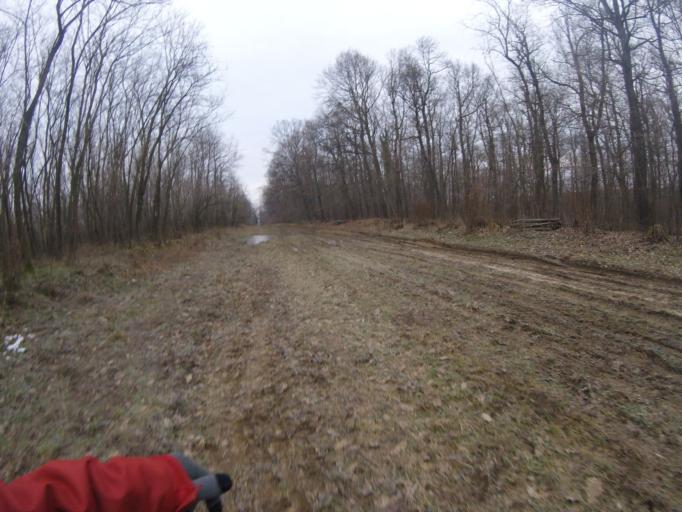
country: HU
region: Baranya
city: Pecsvarad
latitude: 46.1343
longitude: 18.5236
